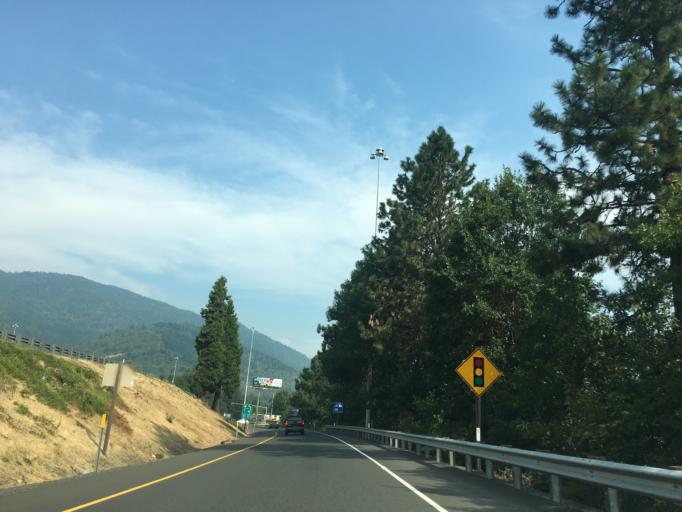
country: US
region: Oregon
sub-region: Jackson County
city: Rogue River
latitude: 42.4307
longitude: -123.1680
